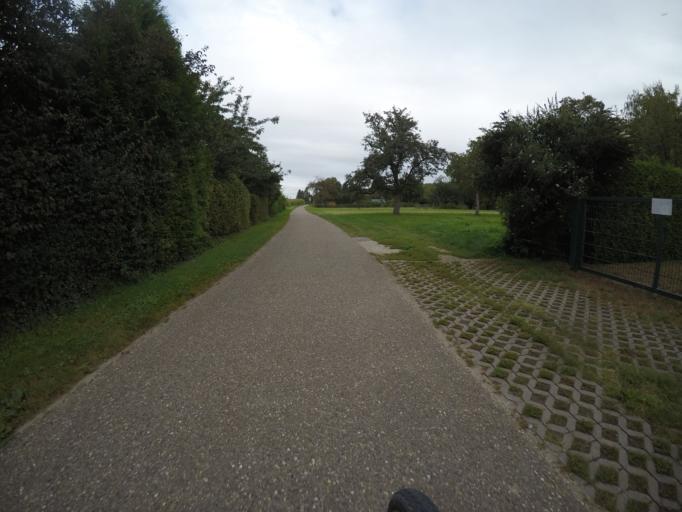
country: DE
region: Baden-Wuerttemberg
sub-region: Regierungsbezirk Stuttgart
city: Erdmannhausen
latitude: 48.8808
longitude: 9.2762
